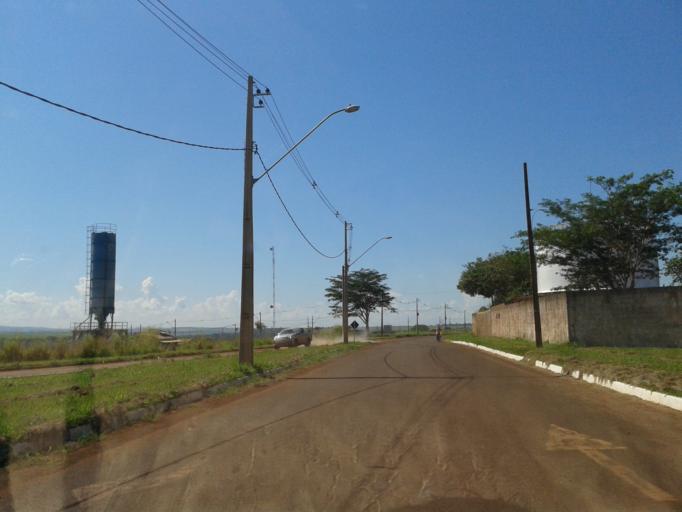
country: BR
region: Goias
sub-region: Itumbiara
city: Itumbiara
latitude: -18.4276
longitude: -49.1875
